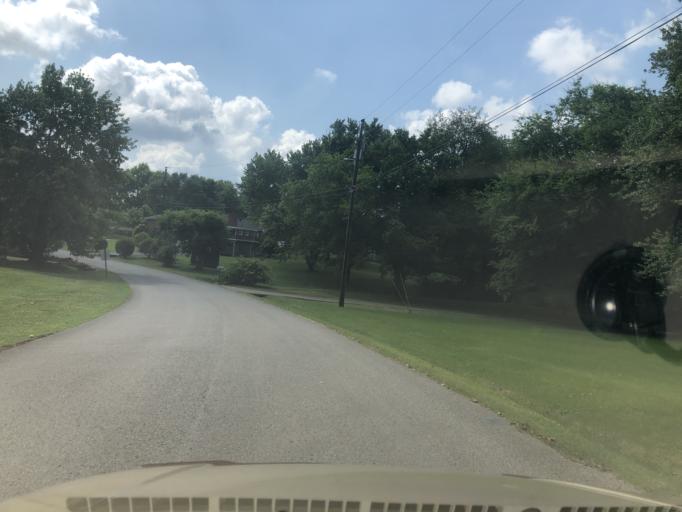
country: US
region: Tennessee
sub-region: Wilson County
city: Green Hill
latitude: 36.2334
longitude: -86.5892
